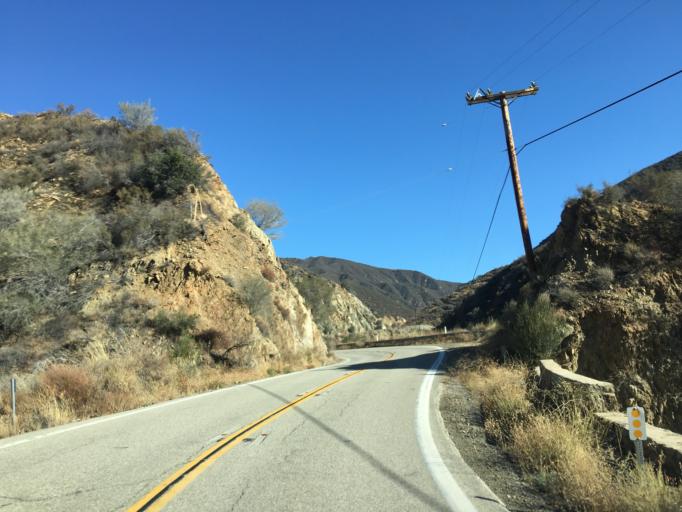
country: US
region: California
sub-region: Los Angeles County
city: Castaic
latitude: 34.5829
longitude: -118.5585
